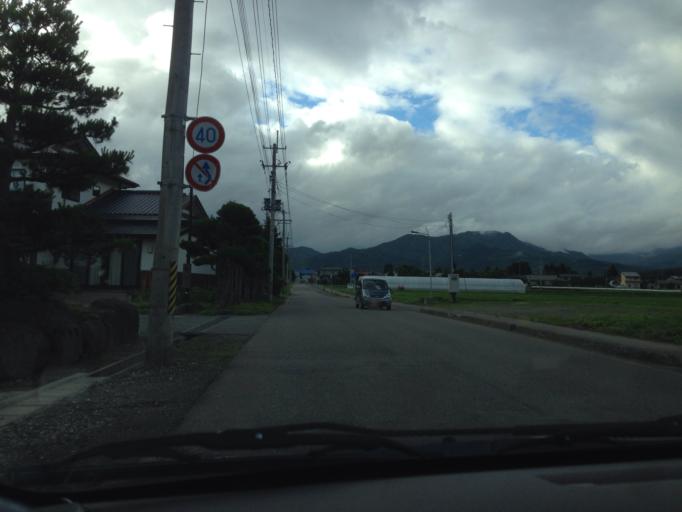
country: JP
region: Fukushima
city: Kitakata
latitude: 37.6928
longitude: 139.8574
